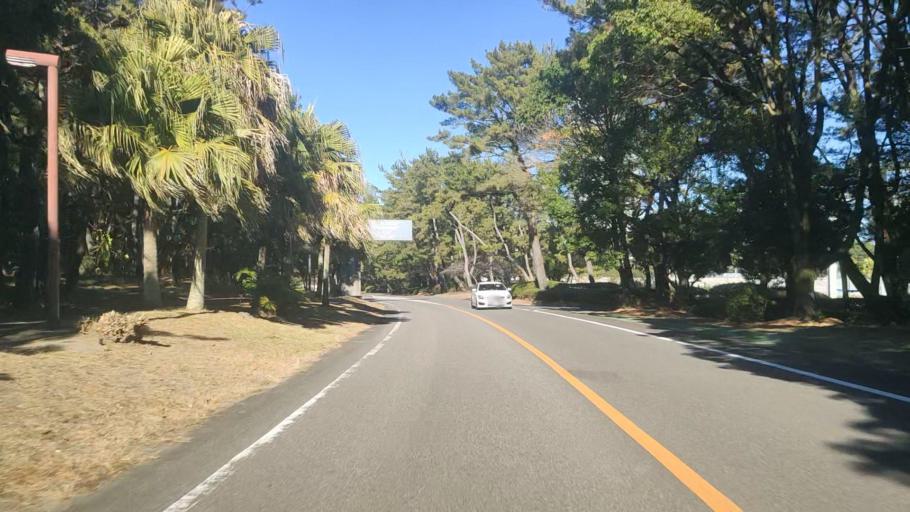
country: JP
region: Miyazaki
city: Miyazaki-shi
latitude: 31.9534
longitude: 131.4670
